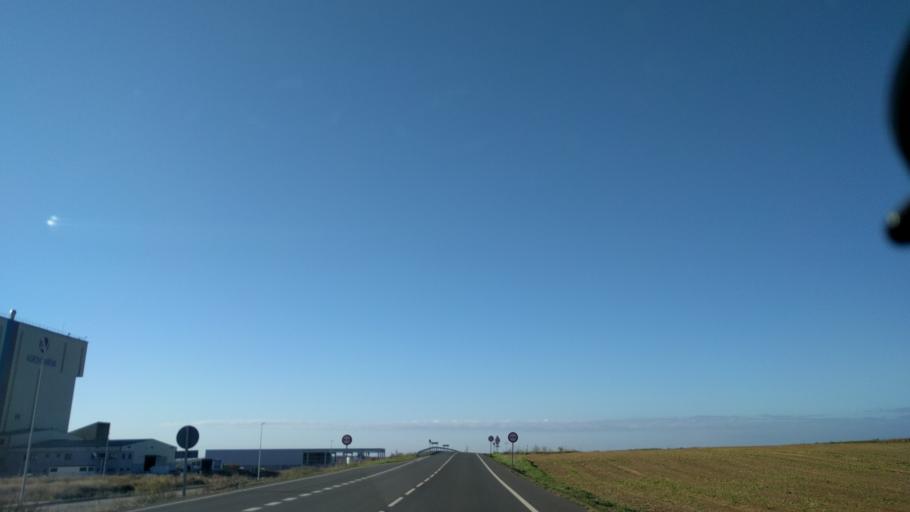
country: ES
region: Catalonia
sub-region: Provincia de Lleida
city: Termens
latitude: 41.6967
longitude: 0.7414
